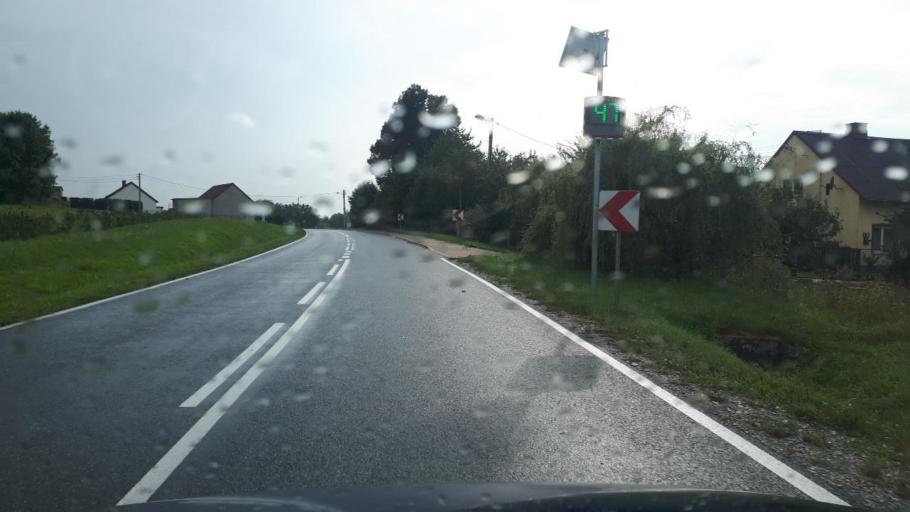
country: PL
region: Silesian Voivodeship
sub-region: Powiat gliwicki
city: Wielowies
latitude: 50.4960
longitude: 18.5915
